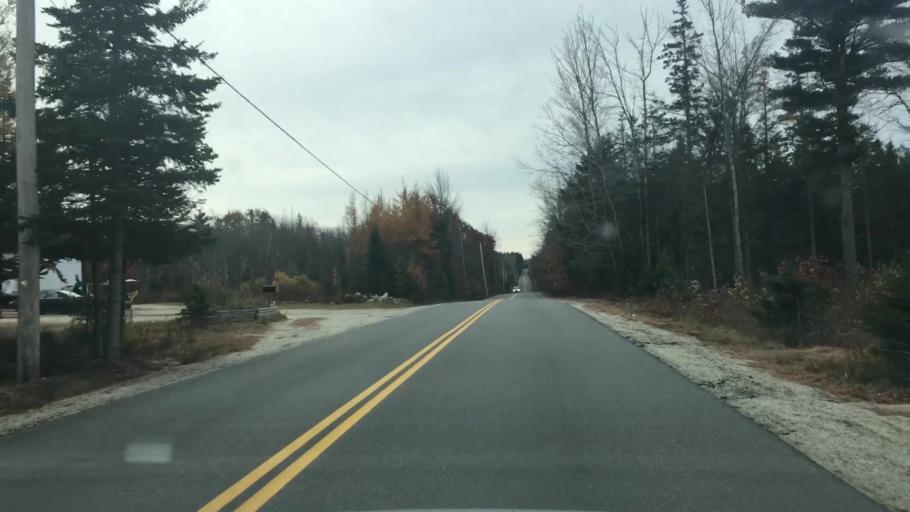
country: US
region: Maine
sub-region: Hancock County
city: Penobscot
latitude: 44.4548
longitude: -68.6375
